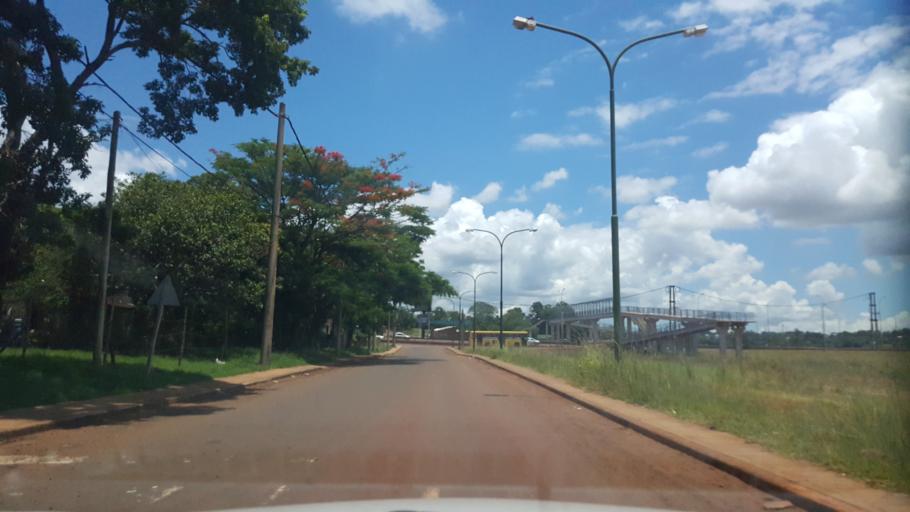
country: AR
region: Misiones
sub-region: Departamento de Capital
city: Posadas
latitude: -27.4213
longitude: -55.8976
